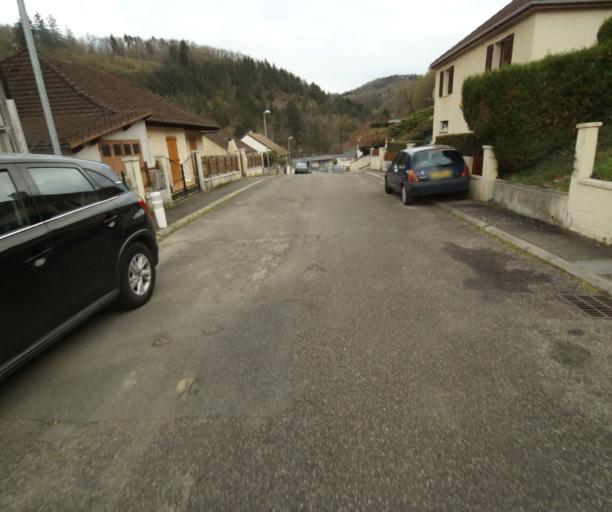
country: FR
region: Limousin
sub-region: Departement de la Correze
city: Laguenne
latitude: 45.2525
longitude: 1.7744
